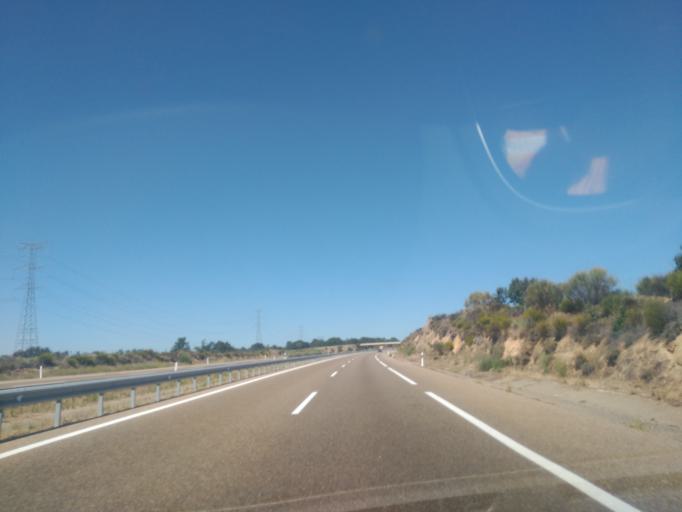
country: ES
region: Castille and Leon
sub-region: Provincia de Zamora
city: Mombuey
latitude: 42.0094
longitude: -6.2842
